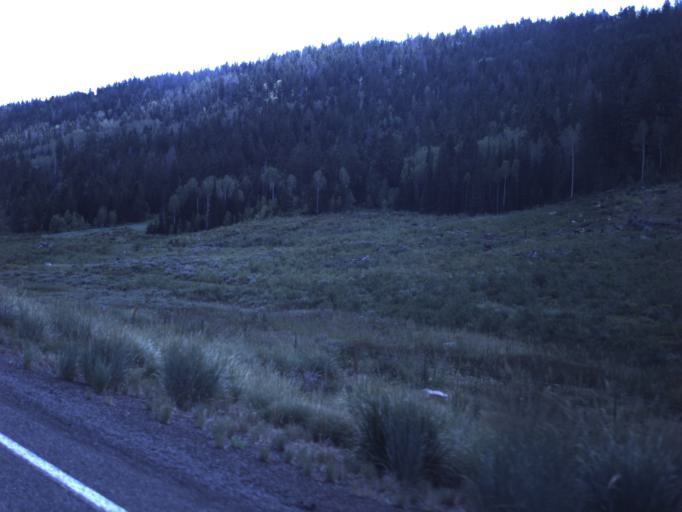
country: US
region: Utah
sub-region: Carbon County
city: Helper
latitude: 39.8570
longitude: -111.0919
